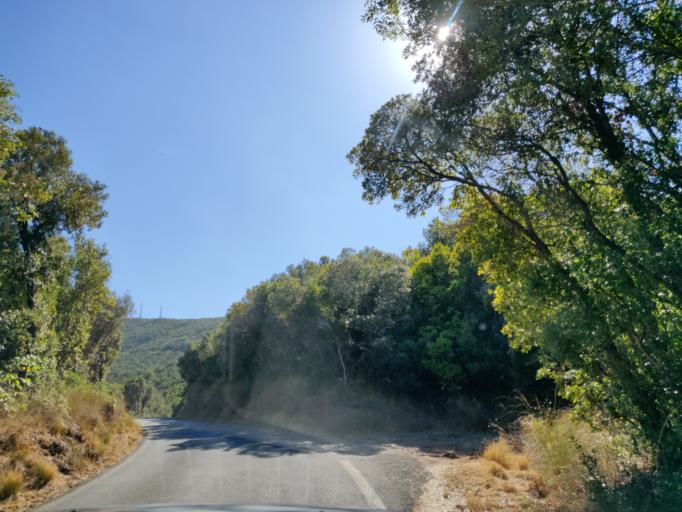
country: IT
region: Tuscany
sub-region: Provincia di Grosseto
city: Monte Argentario
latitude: 42.4177
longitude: 11.1595
